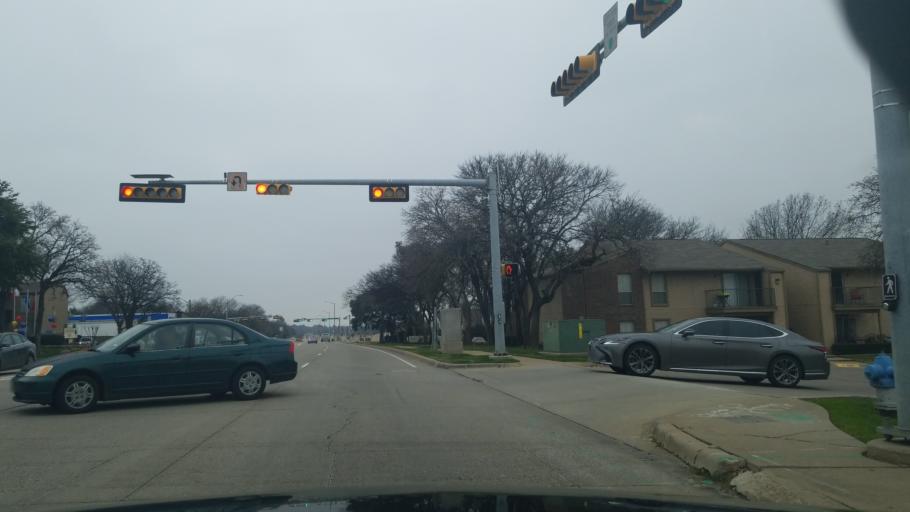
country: US
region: Texas
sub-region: Denton County
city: Denton
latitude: 33.1915
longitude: -97.1245
